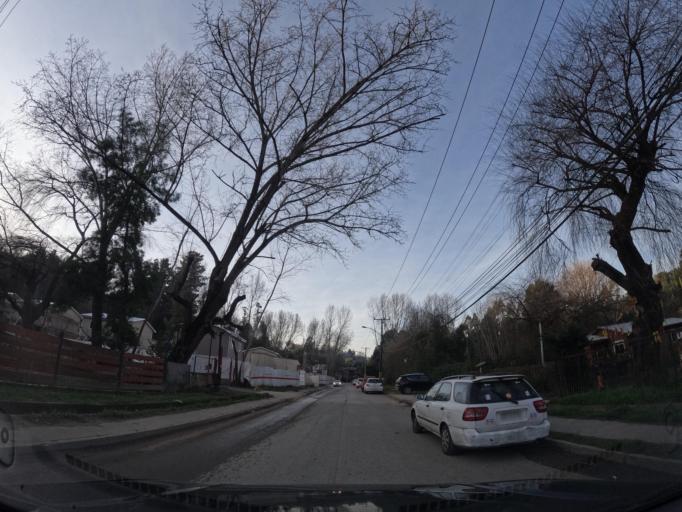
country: CL
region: Biobio
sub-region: Provincia de Concepcion
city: Concepcion
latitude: -36.8425
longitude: -73.0091
